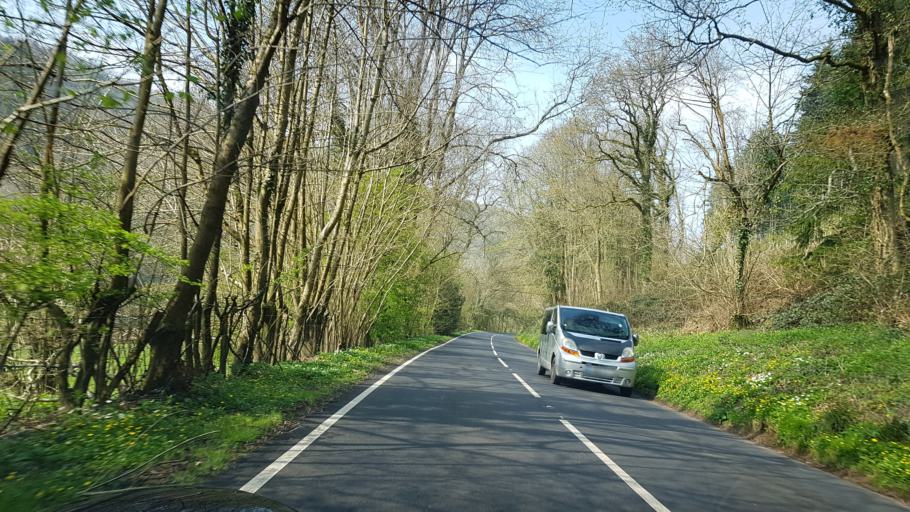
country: GB
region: Wales
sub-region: Monmouthshire
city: Monmouth
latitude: 51.7672
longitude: -2.6784
